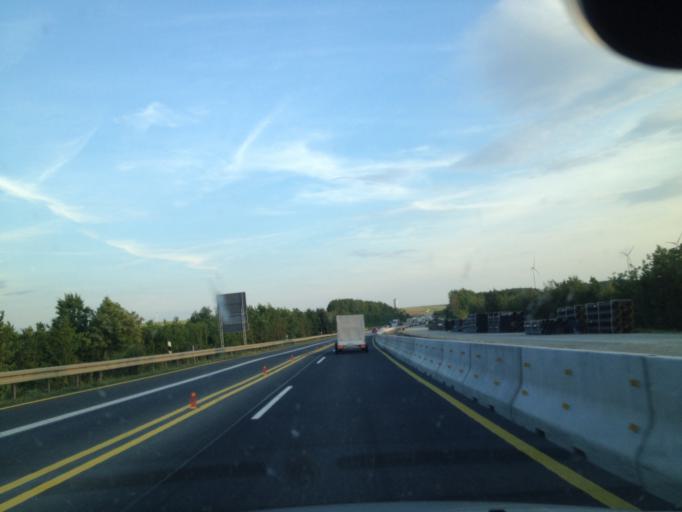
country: DE
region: Bavaria
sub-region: Regierungsbezirk Mittelfranken
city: Gollhofen
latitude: 49.5721
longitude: 10.1726
